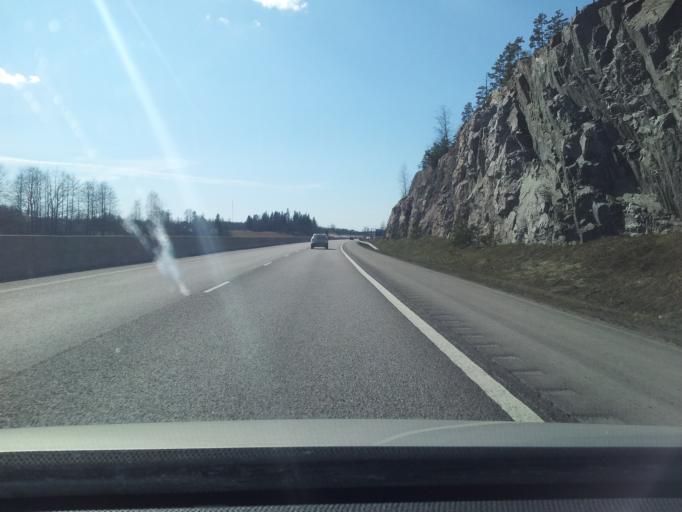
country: FI
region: Uusimaa
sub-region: Loviisa
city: Perna
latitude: 60.4897
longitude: 25.9096
